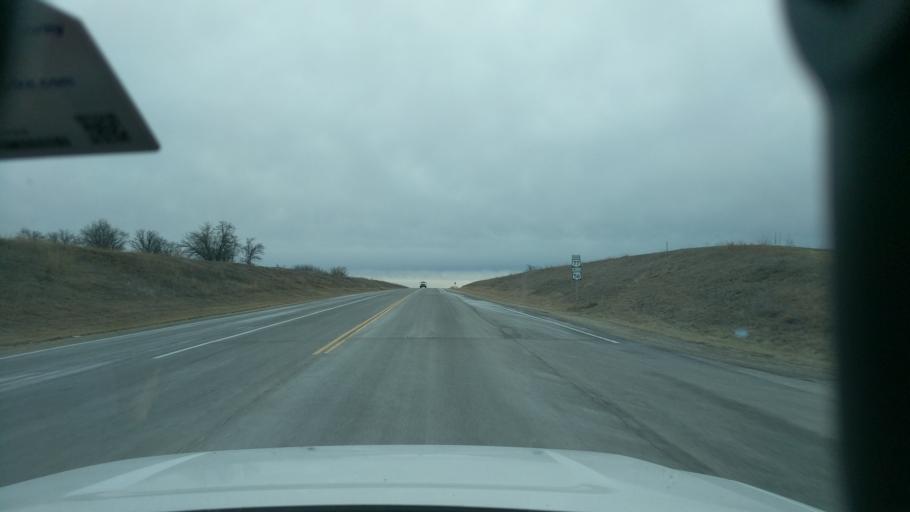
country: US
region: Kansas
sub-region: Marion County
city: Marion
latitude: 38.4354
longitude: -96.9577
